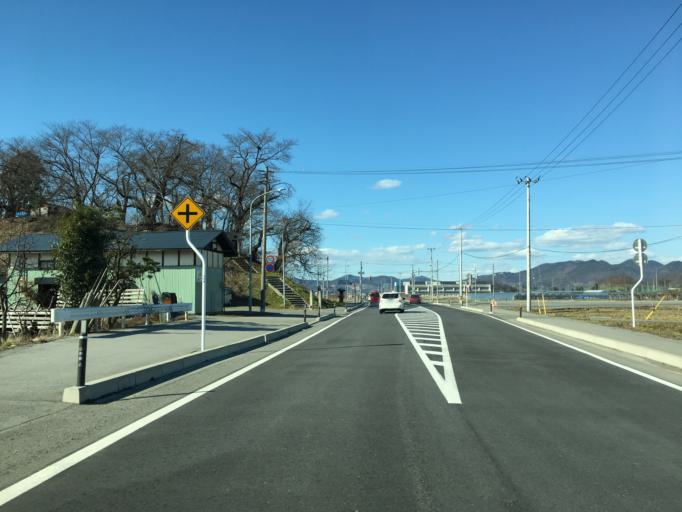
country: JP
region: Yamagata
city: Takahata
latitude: 37.9928
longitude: 140.1788
